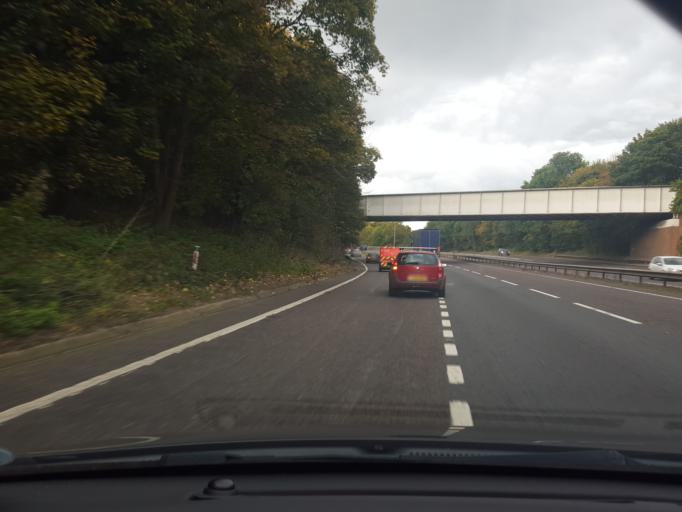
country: GB
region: England
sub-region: Suffolk
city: Bury St Edmunds
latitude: 52.2525
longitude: 0.7212
